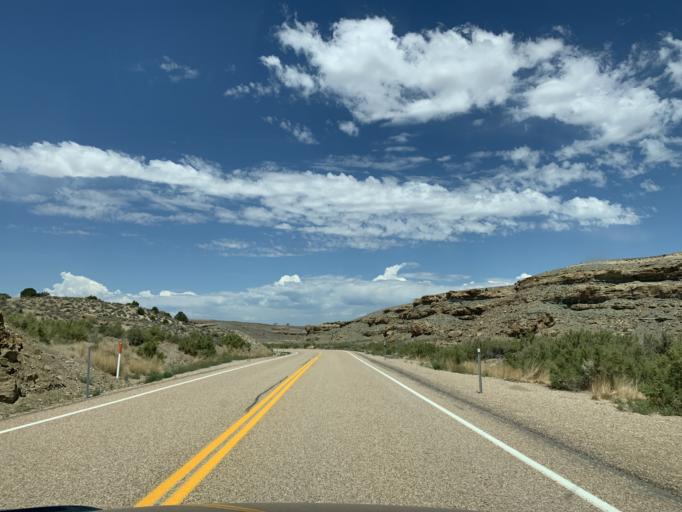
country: US
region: Utah
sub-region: Duchesne County
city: Duchesne
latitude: 40.0133
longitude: -110.1513
